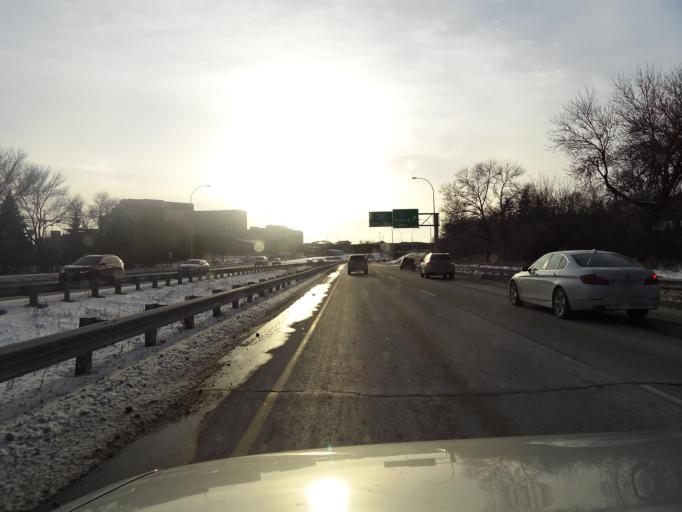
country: US
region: Minnesota
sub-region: Hennepin County
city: Edina
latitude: 44.8889
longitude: -93.3249
